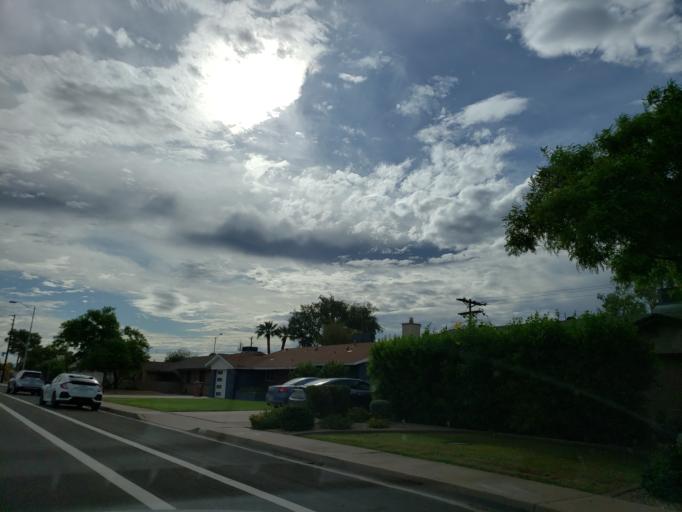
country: US
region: Arizona
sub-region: Maricopa County
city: Scottsdale
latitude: 33.4731
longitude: -111.9059
